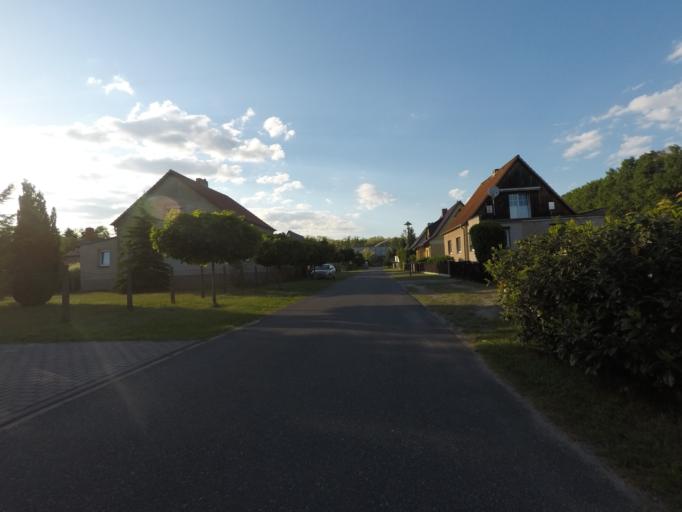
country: DE
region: Brandenburg
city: Marienwerder
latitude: 52.8544
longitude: 13.6725
